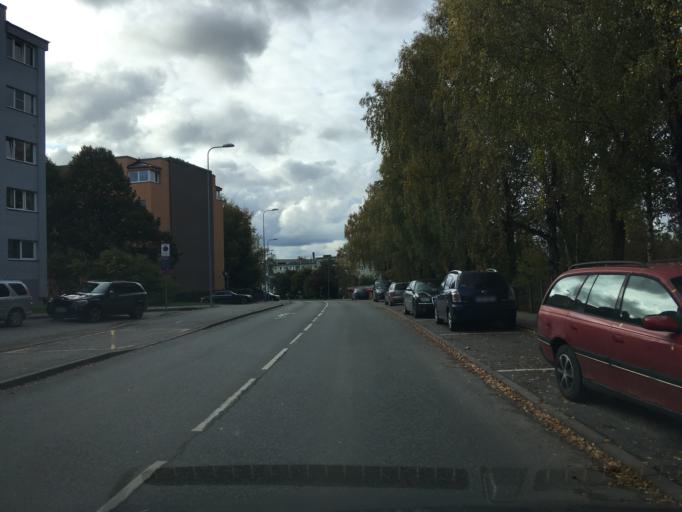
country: EE
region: Harju
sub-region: Tallinna linn
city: Tallinn
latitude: 59.4328
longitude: 24.7958
